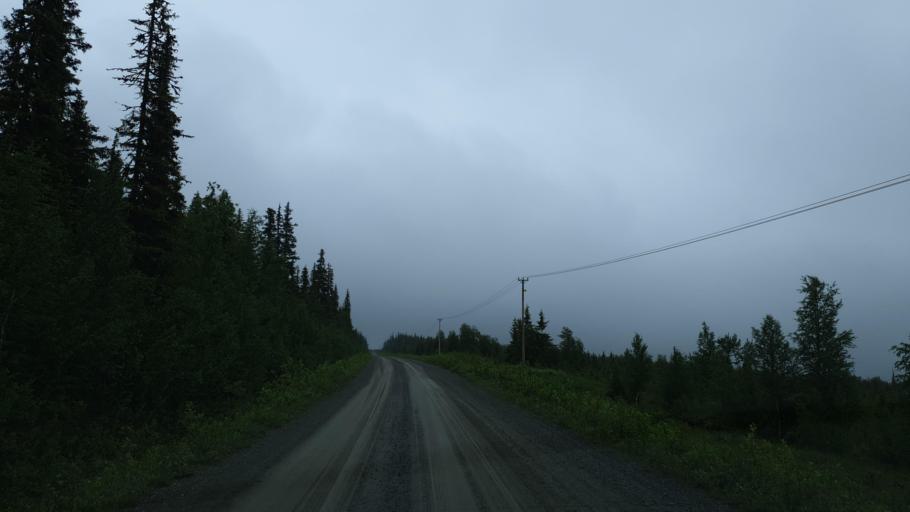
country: SE
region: Vaesterbotten
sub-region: Vilhelmina Kommun
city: Sjoberg
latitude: 65.3224
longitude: 15.9344
